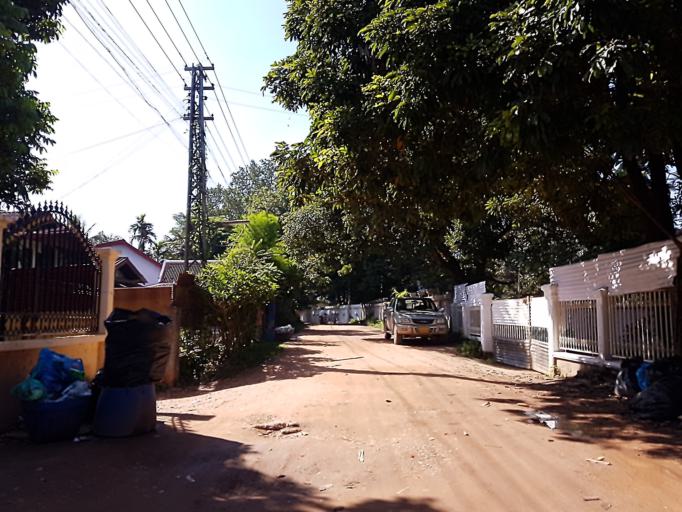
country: TH
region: Nong Khai
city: Si Chiang Mai
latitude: 17.9088
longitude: 102.6176
